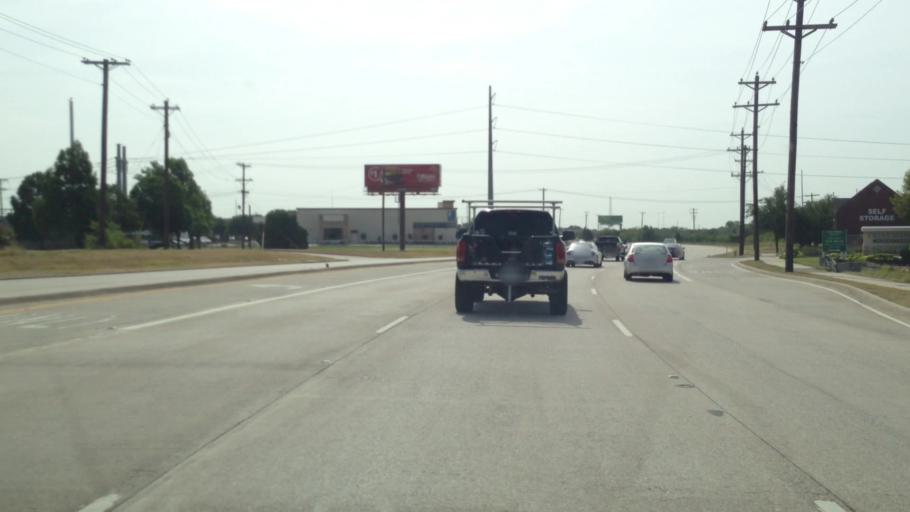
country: US
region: Texas
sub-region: Denton County
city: Lewisville
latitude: 33.0057
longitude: -97.0127
